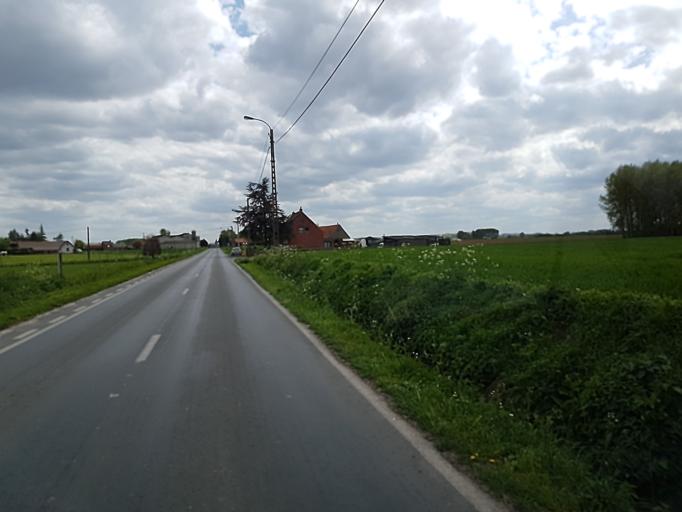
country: BE
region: Wallonia
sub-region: Province du Hainaut
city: Celles
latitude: 50.7318
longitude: 3.4527
